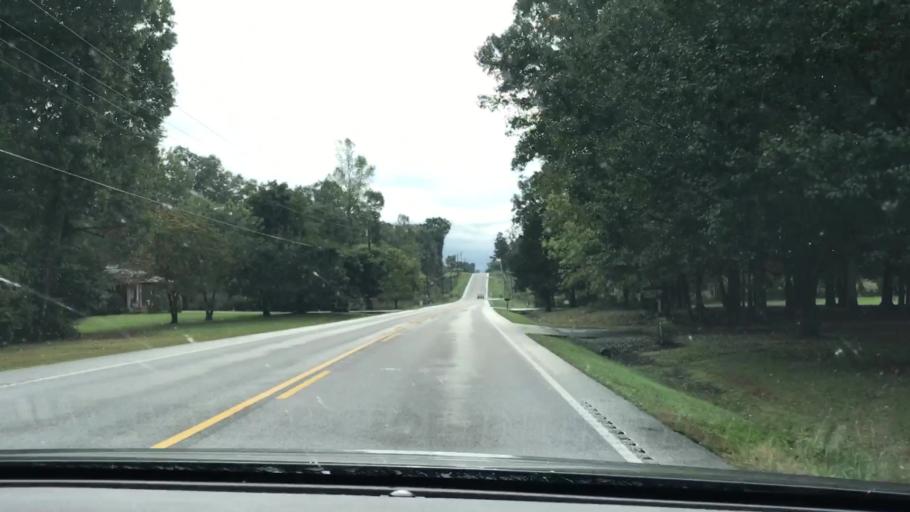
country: US
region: Tennessee
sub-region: Fentress County
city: Jamestown
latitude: 36.3711
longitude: -84.8537
